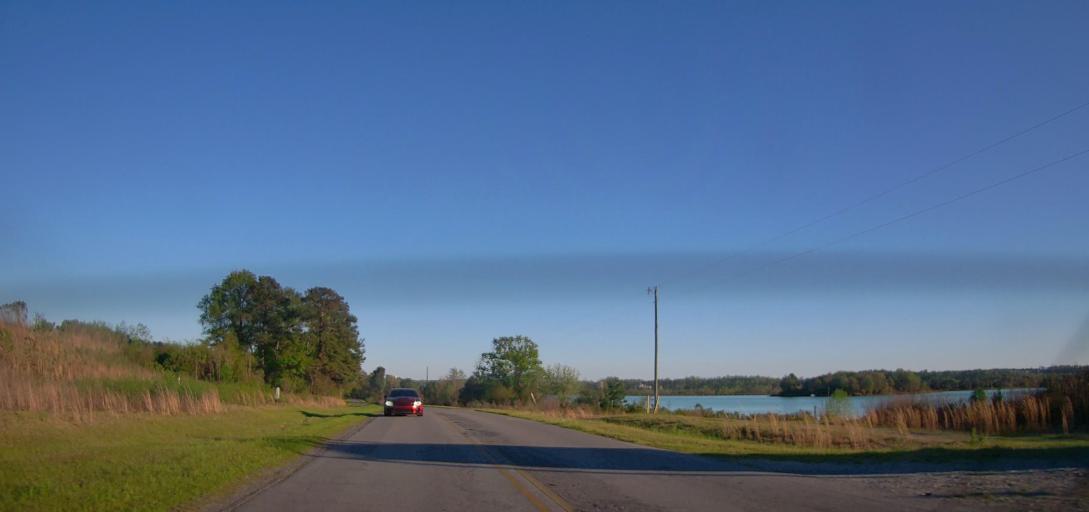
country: US
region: Georgia
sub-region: Wilkinson County
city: Irwinton
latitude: 32.8654
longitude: -83.2334
